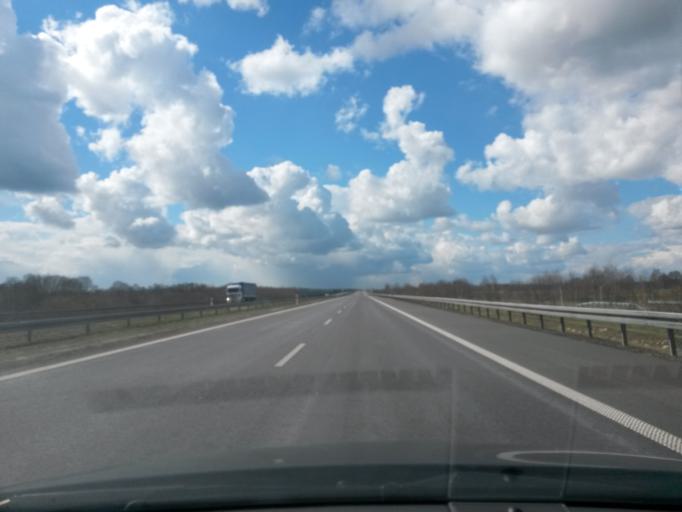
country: PL
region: Greater Poland Voivodeship
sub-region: Powiat kolski
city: Grzegorzew
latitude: 52.1197
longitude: 18.7077
